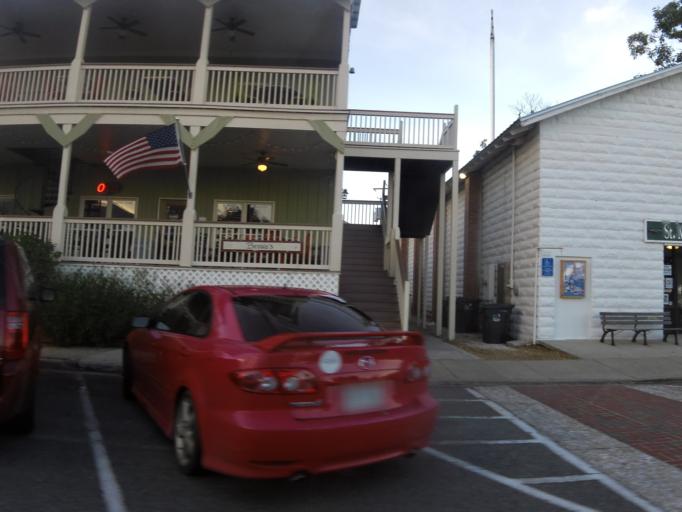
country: US
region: Georgia
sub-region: Camden County
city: St. Marys
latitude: 30.7206
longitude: -81.5493
